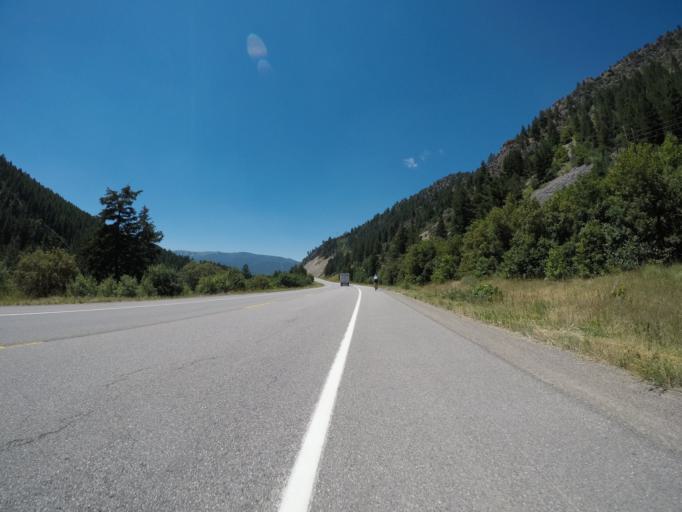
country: US
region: Wyoming
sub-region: Teton County
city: Hoback
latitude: 43.1777
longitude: -110.9902
